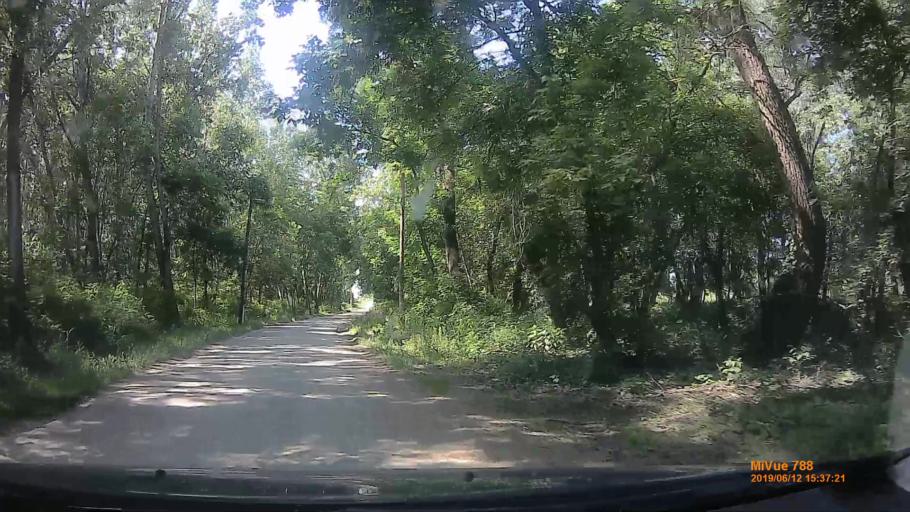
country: HU
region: Csongrad
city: Mako
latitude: 46.2051
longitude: 20.4646
